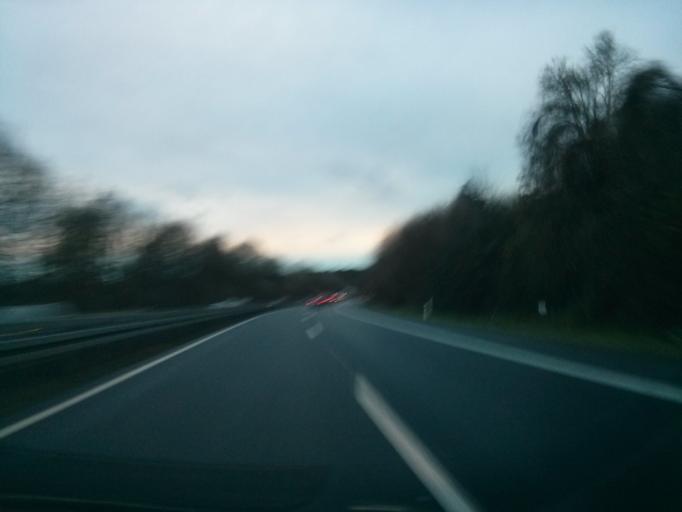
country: DE
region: Hesse
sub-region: Regierungsbezirk Darmstadt
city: Rodgau
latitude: 50.0076
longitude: 8.8980
